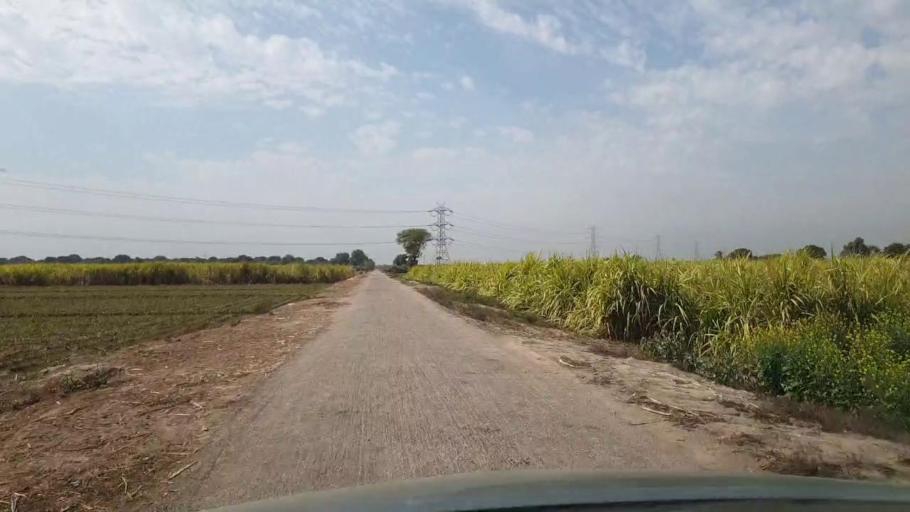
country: PK
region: Sindh
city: Tando Jam
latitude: 25.5617
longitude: 68.6024
